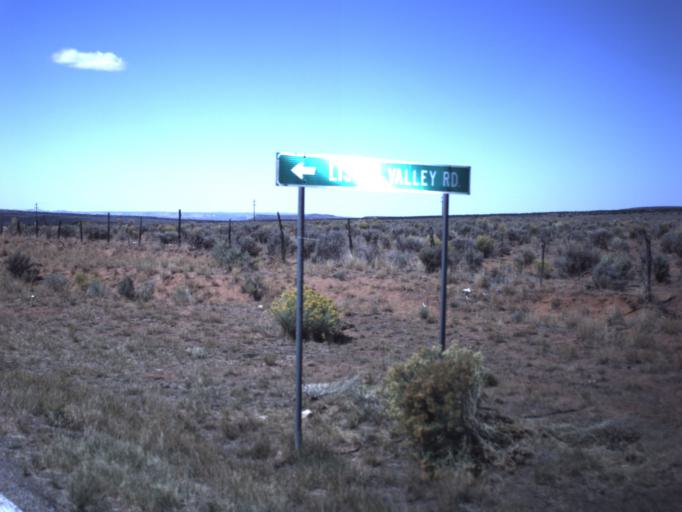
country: US
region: Utah
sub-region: Grand County
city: Moab
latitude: 38.3094
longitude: -109.2919
